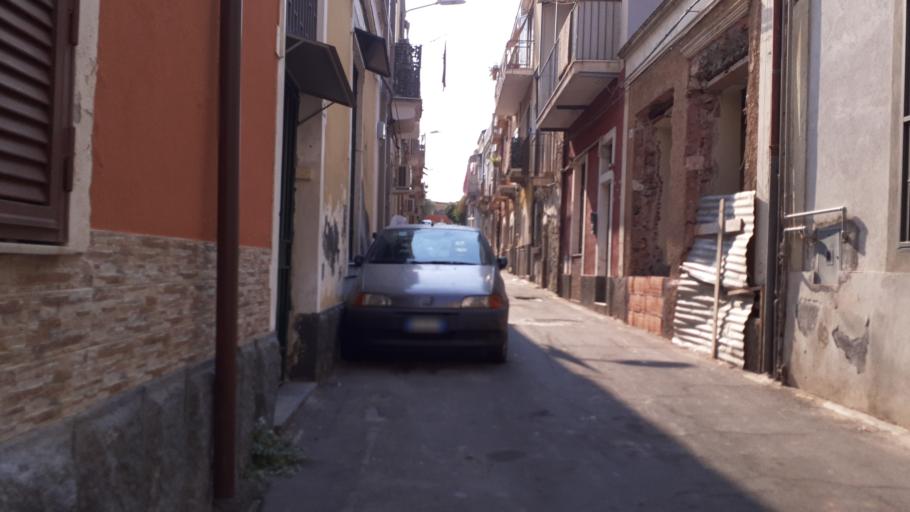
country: IT
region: Sicily
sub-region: Catania
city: Catania
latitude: 37.5070
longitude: 15.0783
